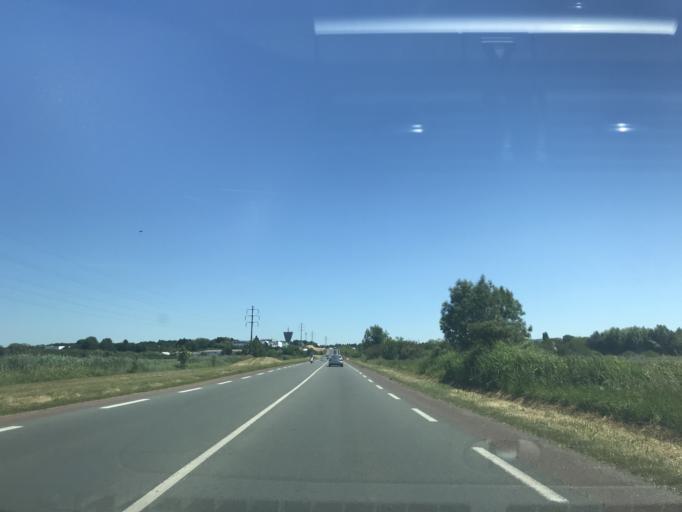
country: FR
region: Poitou-Charentes
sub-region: Departement de la Charente-Maritime
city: Royan
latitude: 45.6336
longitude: -1.0120
